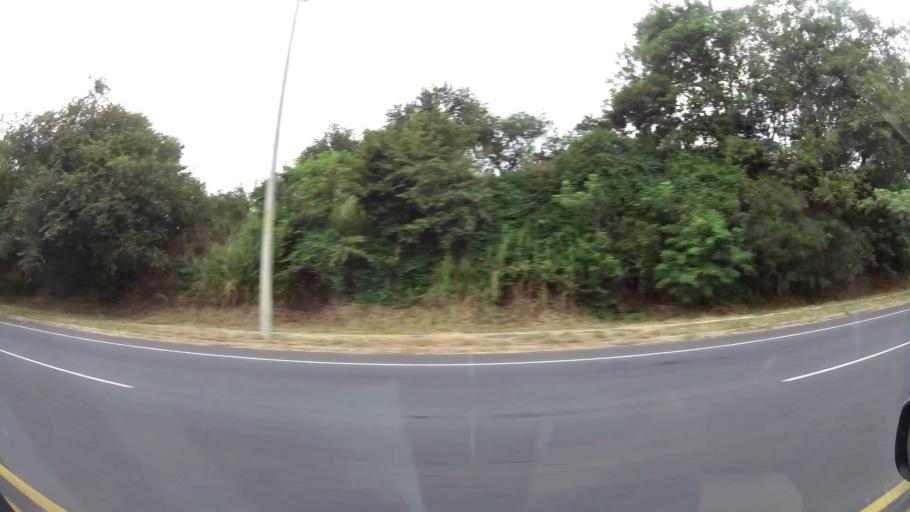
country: CR
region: Puntarenas
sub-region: Canton Central de Puntarenas
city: Chacarita
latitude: 9.9488
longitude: -84.7289
